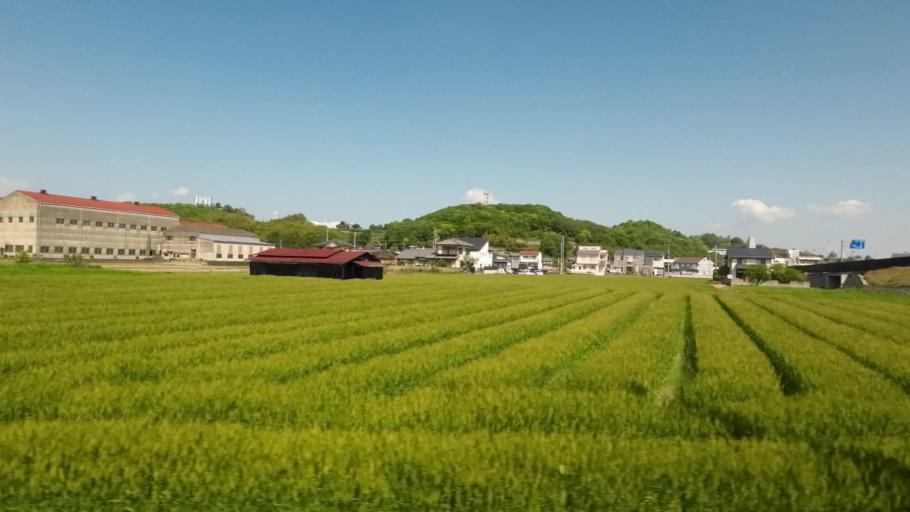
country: JP
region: Kagawa
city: Tadotsu
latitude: 34.2607
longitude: 133.7510
